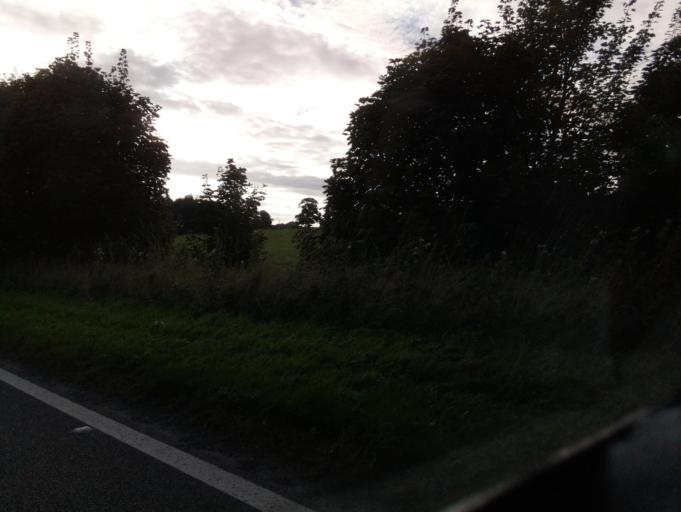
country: GB
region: Scotland
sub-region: Fife
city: Newport-On-Tay
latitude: 56.4227
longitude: -2.9412
